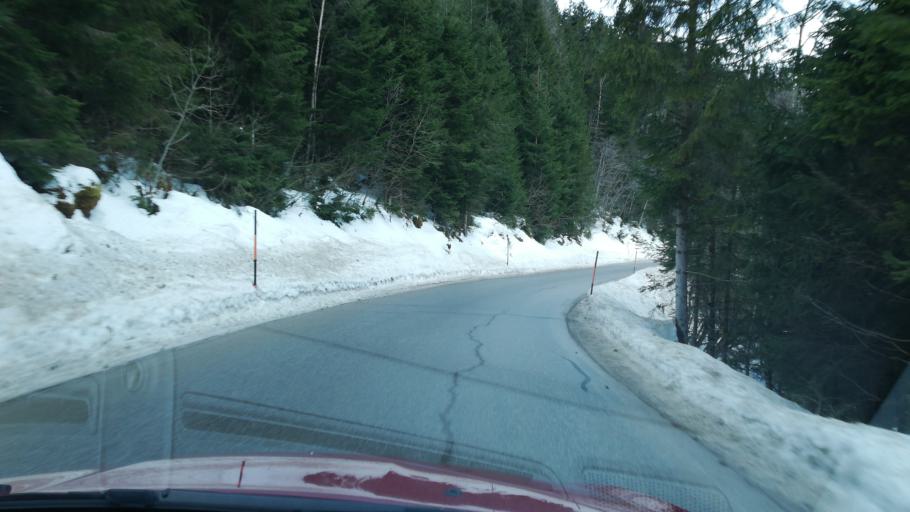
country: AT
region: Styria
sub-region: Politischer Bezirk Liezen
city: Donnersbach
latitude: 47.4242
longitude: 14.1656
